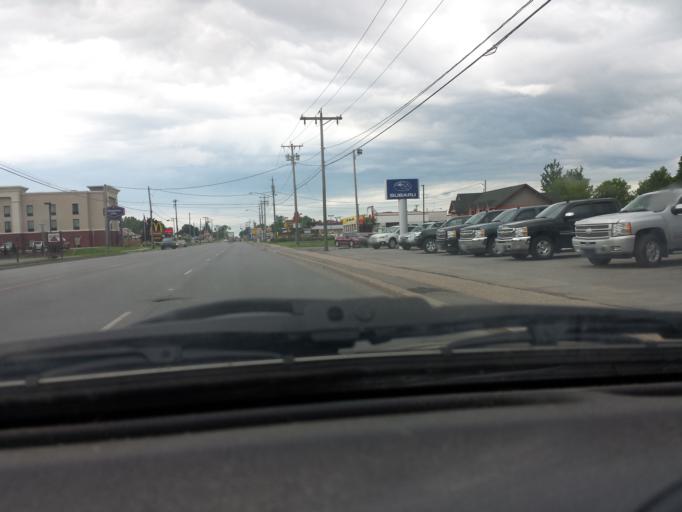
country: US
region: New York
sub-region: St. Lawrence County
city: Potsdam
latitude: 44.6813
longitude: -74.9869
